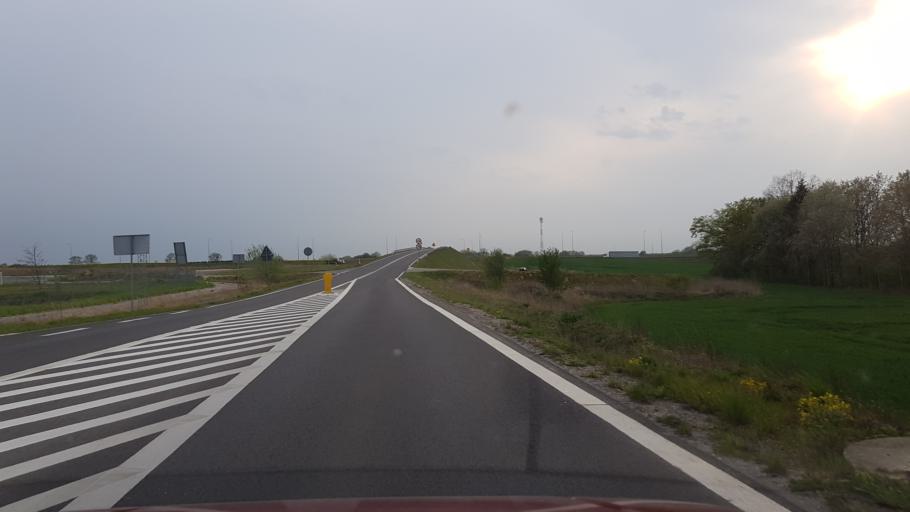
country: PL
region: West Pomeranian Voivodeship
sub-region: Powiat pyrzycki
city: Bielice
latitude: 53.2629
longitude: 14.6353
